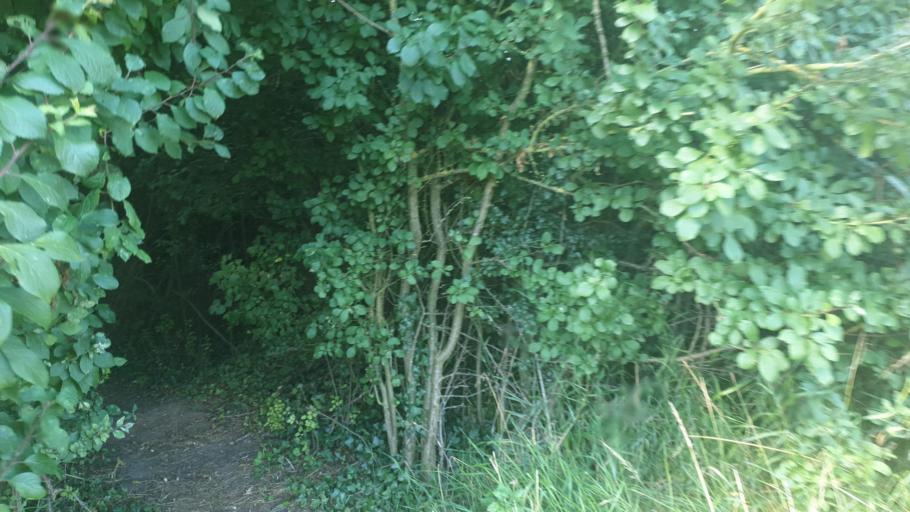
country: GB
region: England
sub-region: Suffolk
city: Shotley Gate
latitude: 51.9229
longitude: 1.2161
